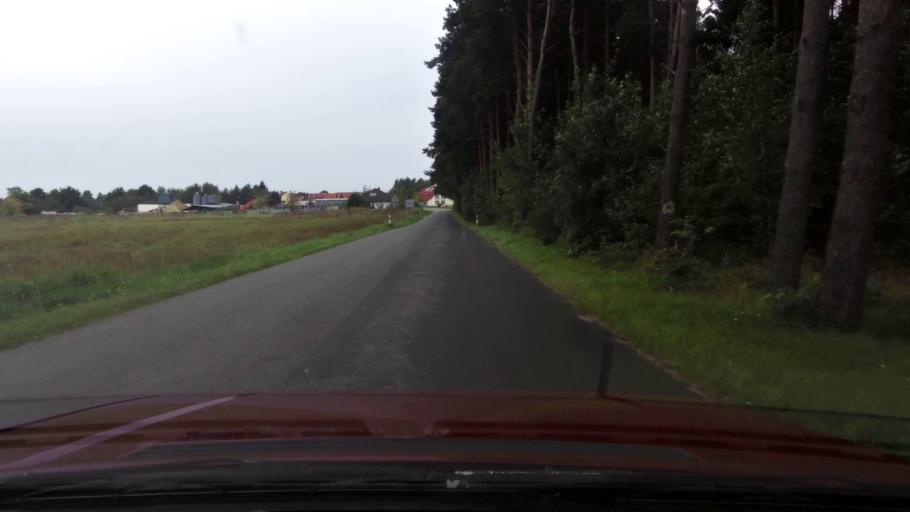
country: PL
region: West Pomeranian Voivodeship
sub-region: Powiat kolobrzeski
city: Grzybowo
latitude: 54.1532
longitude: 15.5001
